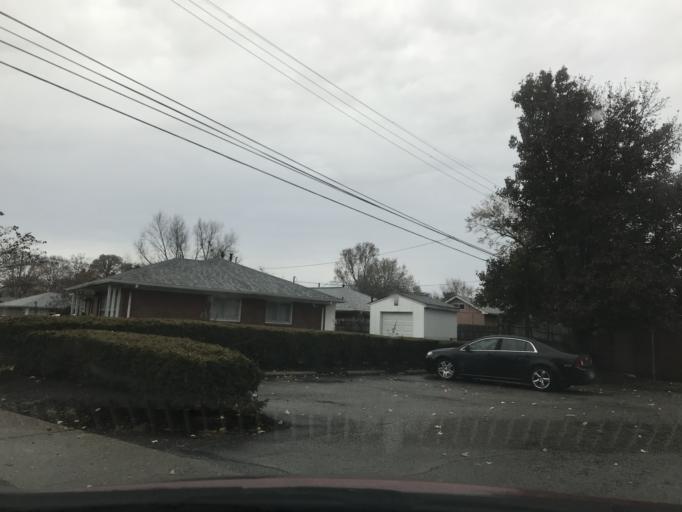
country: US
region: Kentucky
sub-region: Jefferson County
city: West Buechel
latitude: 38.2150
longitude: -85.6557
